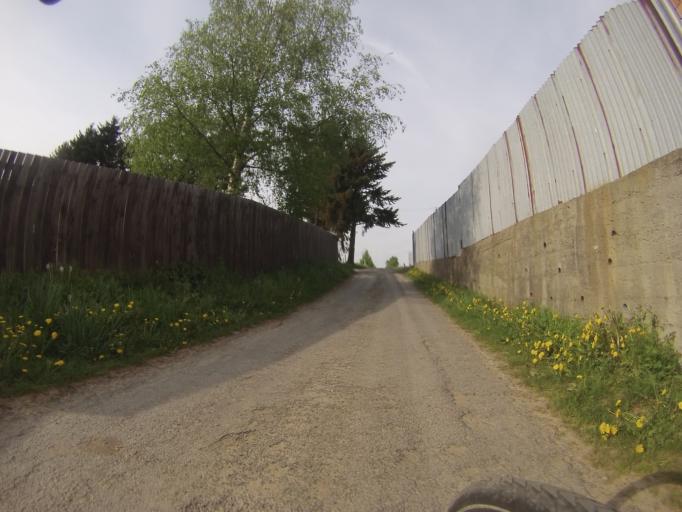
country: CZ
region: Olomoucky
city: Protivanov
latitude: 49.4425
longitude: 16.8568
